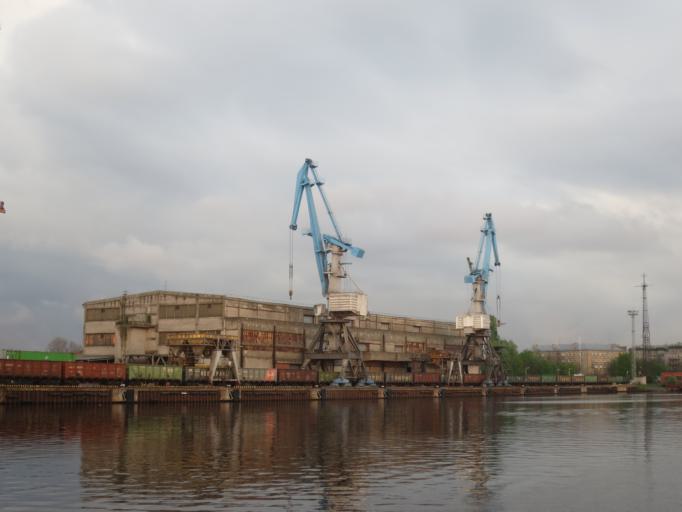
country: LV
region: Riga
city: Riga
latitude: 56.9739
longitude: 24.0923
